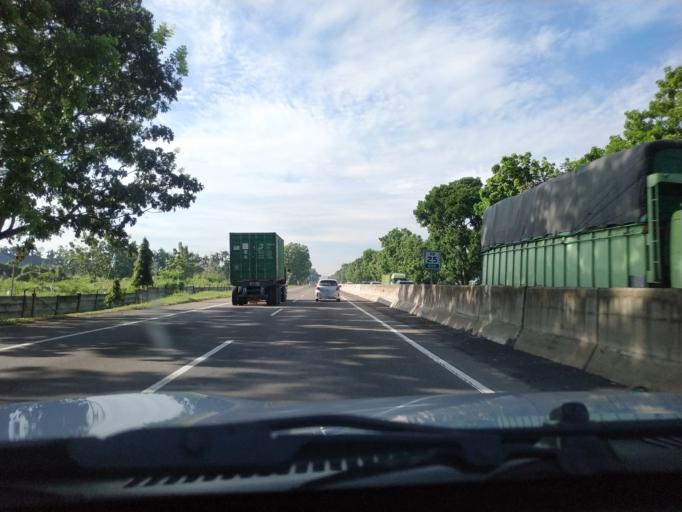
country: ID
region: North Sumatra
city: Medan
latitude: 3.5620
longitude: 98.7257
